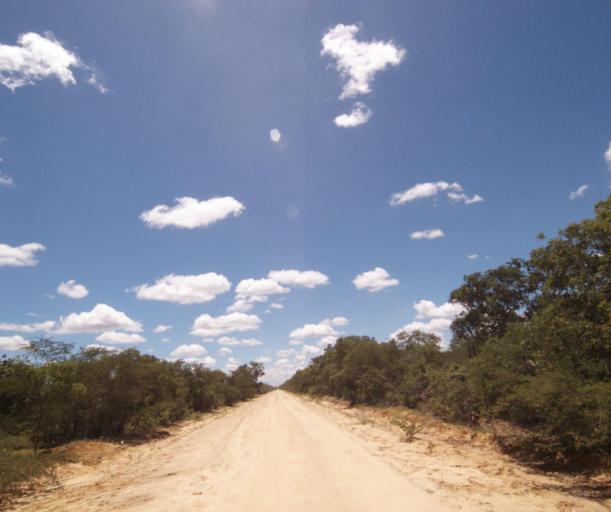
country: BR
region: Bahia
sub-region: Carinhanha
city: Carinhanha
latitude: -14.2088
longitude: -43.9472
